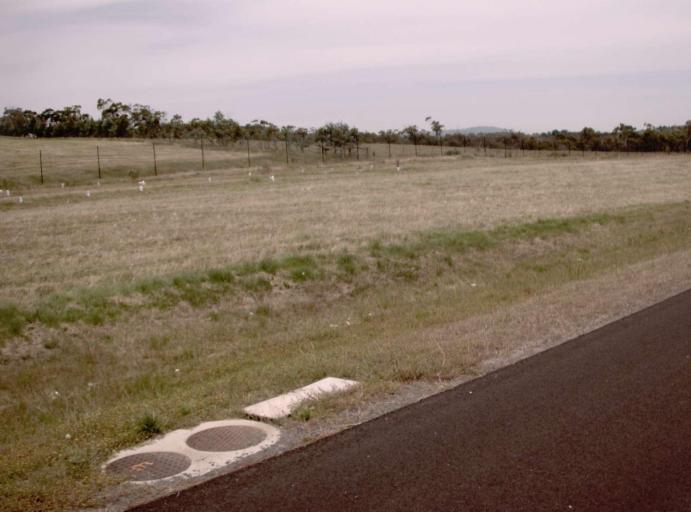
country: AU
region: Victoria
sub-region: Mornington Peninsula
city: Moorooduc
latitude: -38.2713
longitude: 145.0857
